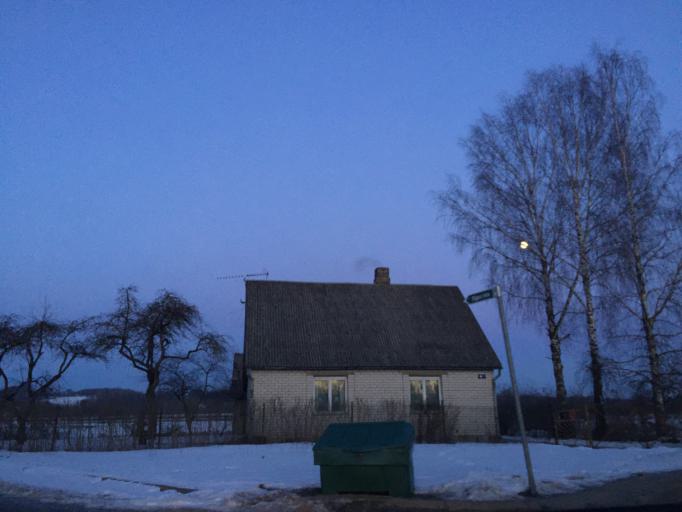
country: LV
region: Jaunjelgava
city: Jaunjelgava
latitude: 56.6192
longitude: 25.0891
